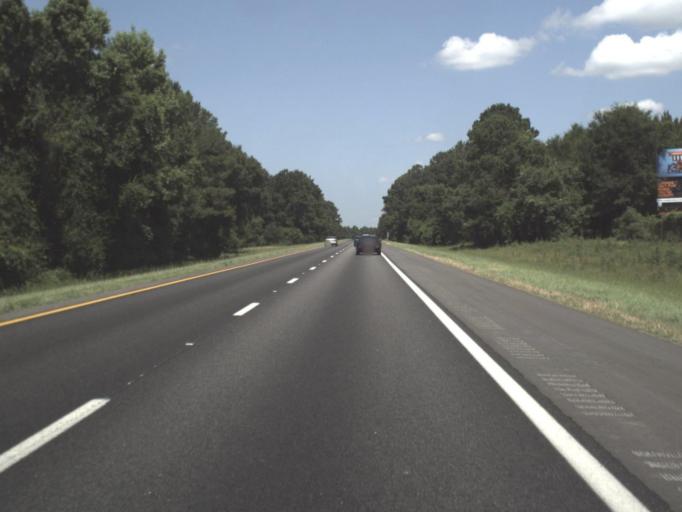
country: US
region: Florida
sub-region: Madison County
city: Madison
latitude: 30.4110
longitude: -83.4205
